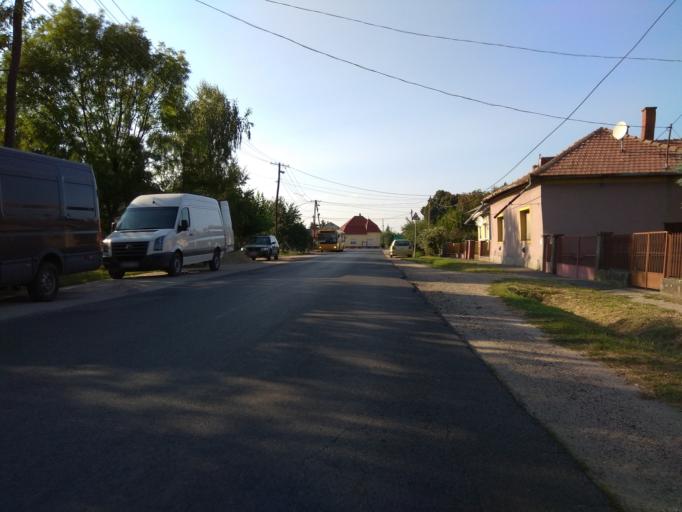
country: HU
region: Borsod-Abauj-Zemplen
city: Onod
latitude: 48.0015
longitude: 20.9178
